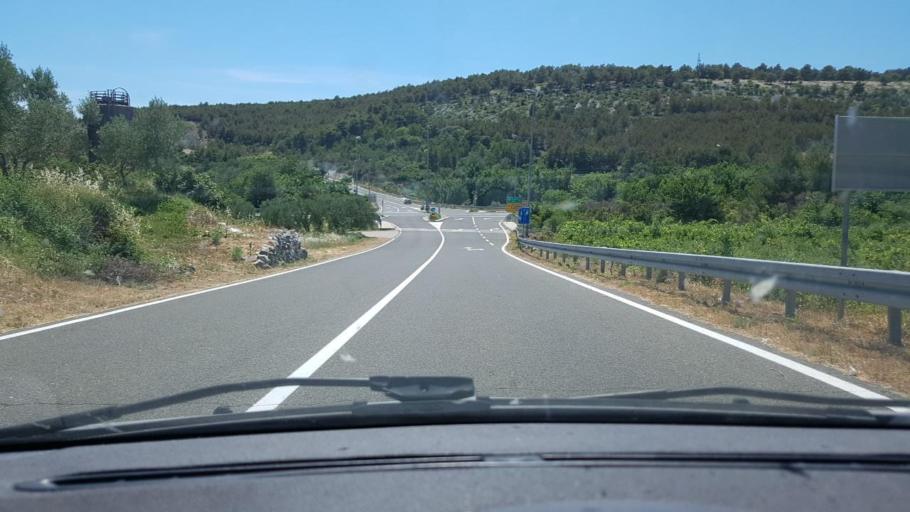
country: HR
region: Sibensko-Kniniska
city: Zaton
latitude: 43.8436
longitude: 15.9004
